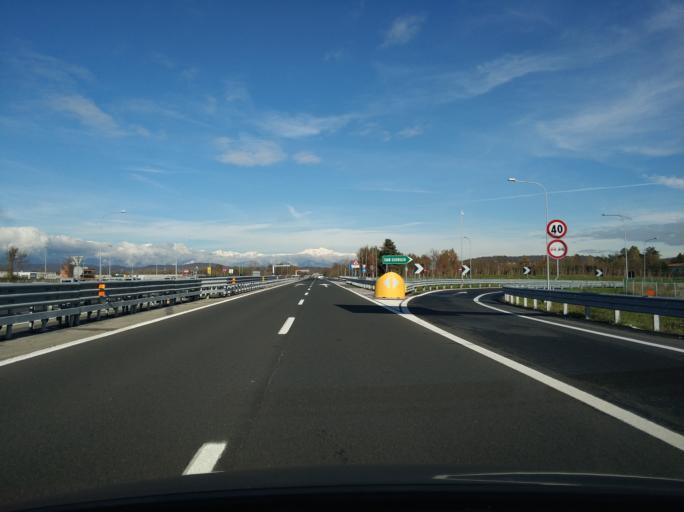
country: IT
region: Piedmont
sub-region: Provincia di Torino
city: San Giusto Canavese
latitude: 45.3147
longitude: 7.8203
